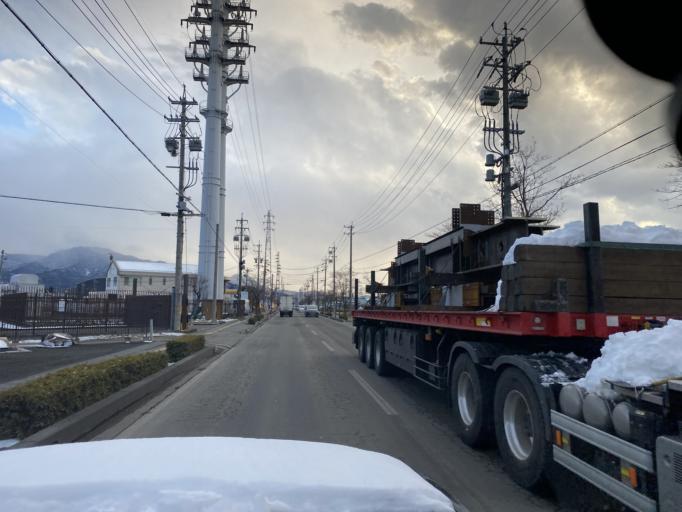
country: JP
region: Nagano
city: Nagano-shi
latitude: 36.6374
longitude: 138.2414
